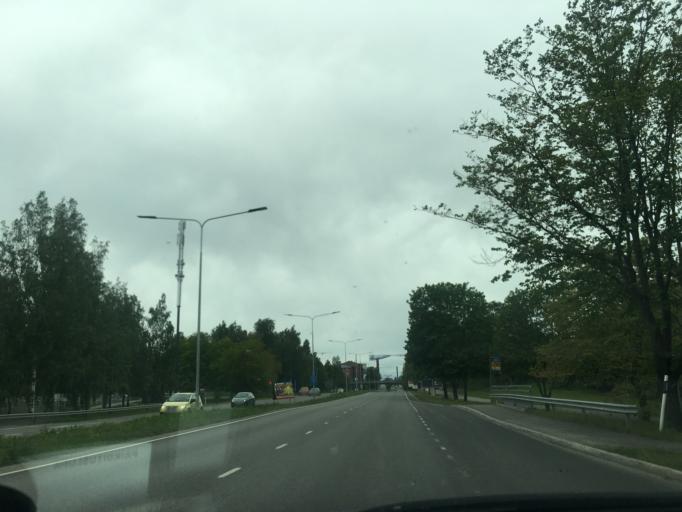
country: FI
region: Varsinais-Suomi
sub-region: Turku
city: Turku
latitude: 60.4586
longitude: 22.3082
